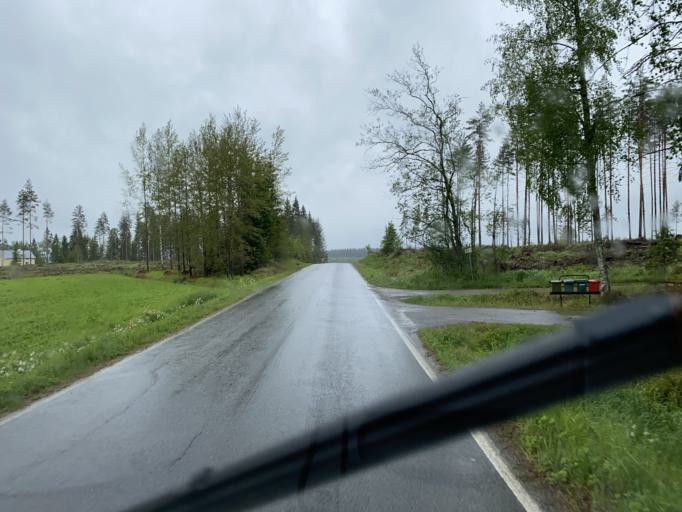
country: FI
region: Haeme
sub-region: Forssa
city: Humppila
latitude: 61.0584
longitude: 23.3254
